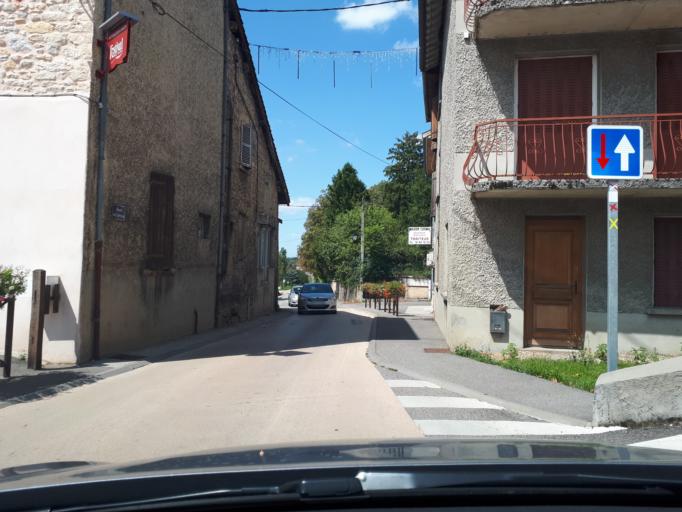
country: FR
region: Rhone-Alpes
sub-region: Departement de l'Isere
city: Frontonas
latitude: 45.6489
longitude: 5.1838
